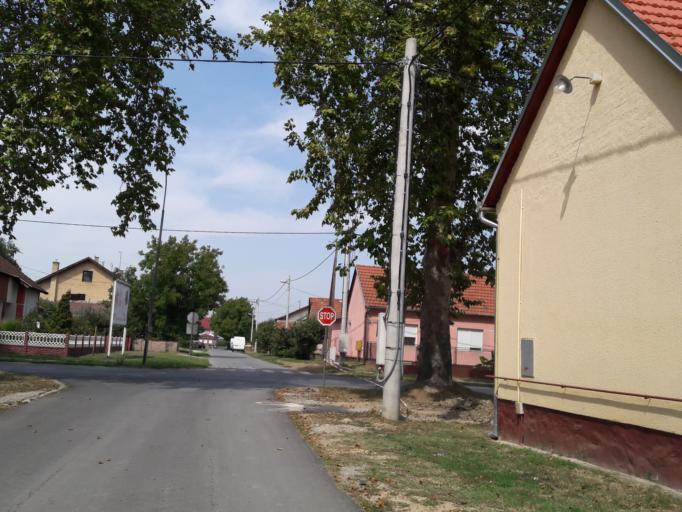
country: HR
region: Osjecko-Baranjska
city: Visnjevac
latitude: 45.5298
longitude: 18.6157
